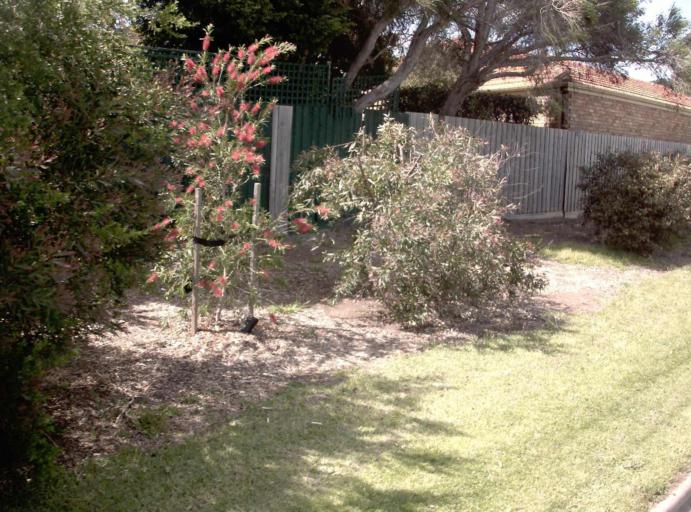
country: AU
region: Victoria
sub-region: Manningham
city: Donvale
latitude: -37.7728
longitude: 145.1650
